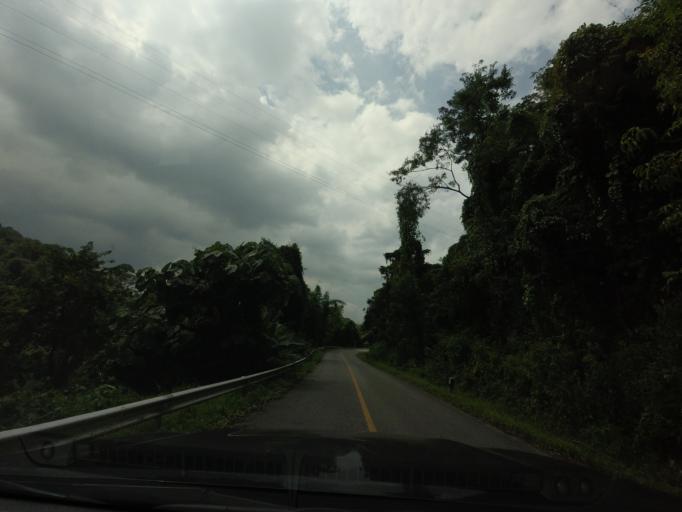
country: TH
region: Loei
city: Na Haeo
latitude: 17.7032
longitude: 100.9485
